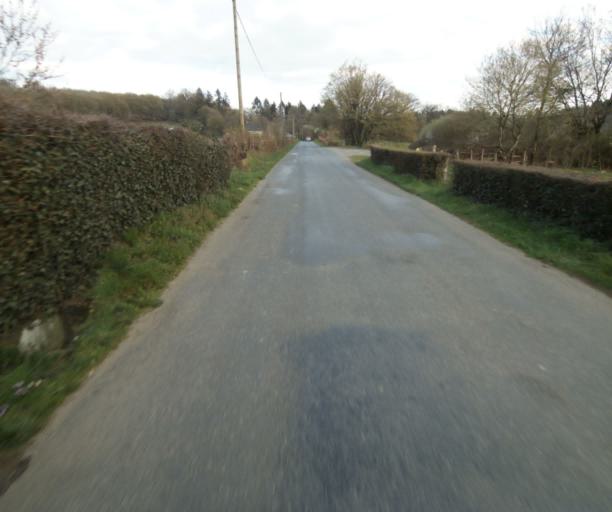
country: FR
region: Limousin
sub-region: Departement de la Correze
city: Saint-Clement
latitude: 45.3603
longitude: 1.6280
